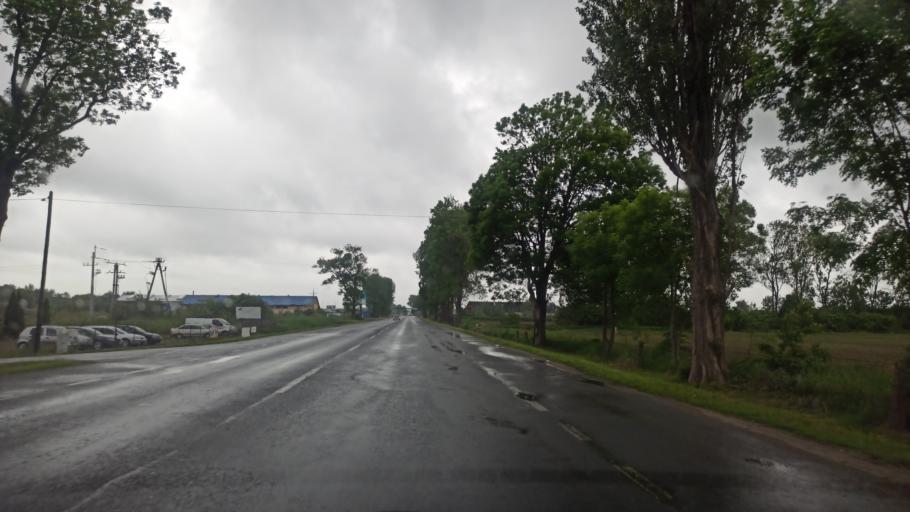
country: PL
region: Subcarpathian Voivodeship
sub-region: Powiat jaroslawski
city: Radymno
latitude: 49.9570
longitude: 22.8094
